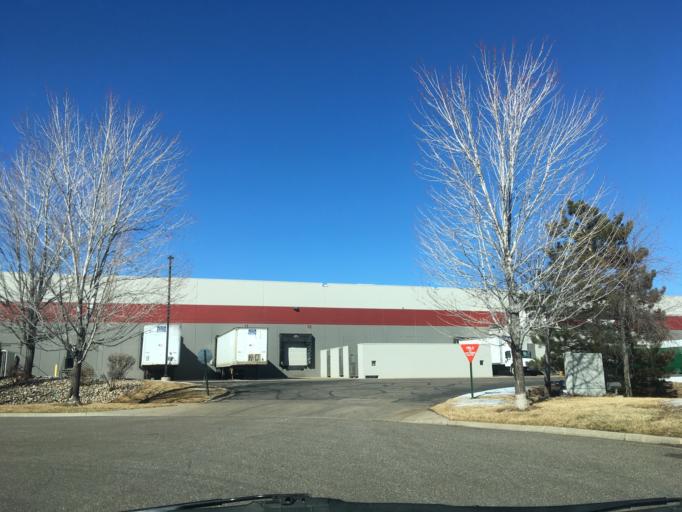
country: US
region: Colorado
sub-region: Boulder County
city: Louisville
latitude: 39.9664
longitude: -105.1225
